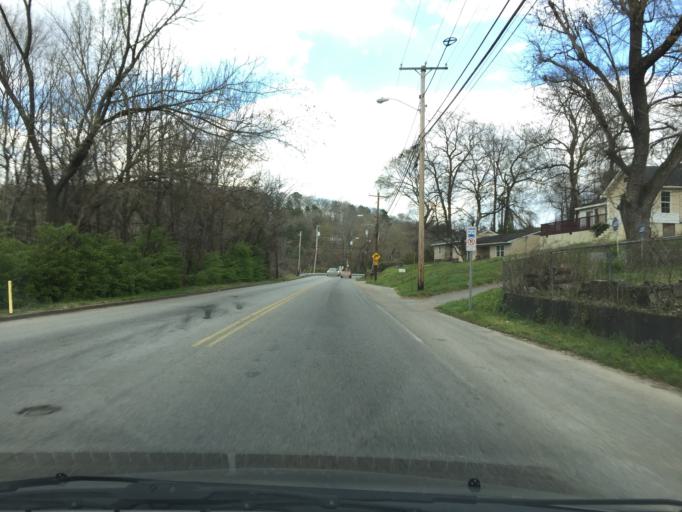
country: US
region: Tennessee
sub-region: Hamilton County
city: East Chattanooga
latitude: 35.0724
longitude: -85.2414
